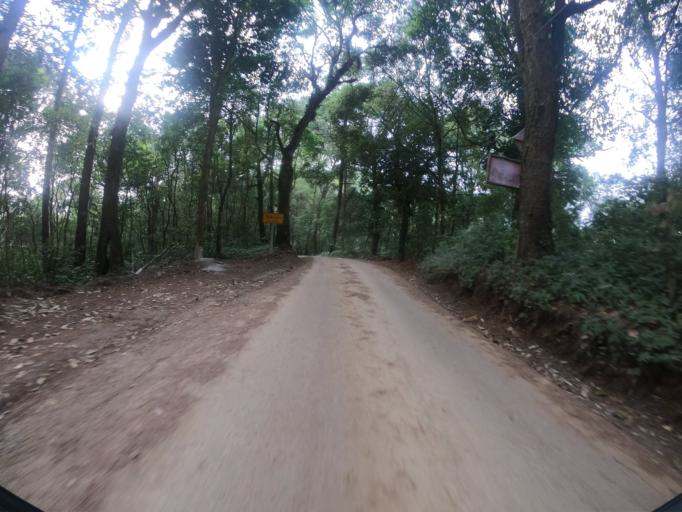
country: TH
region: Chiang Mai
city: Chiang Mai
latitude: 18.8214
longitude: 98.8908
